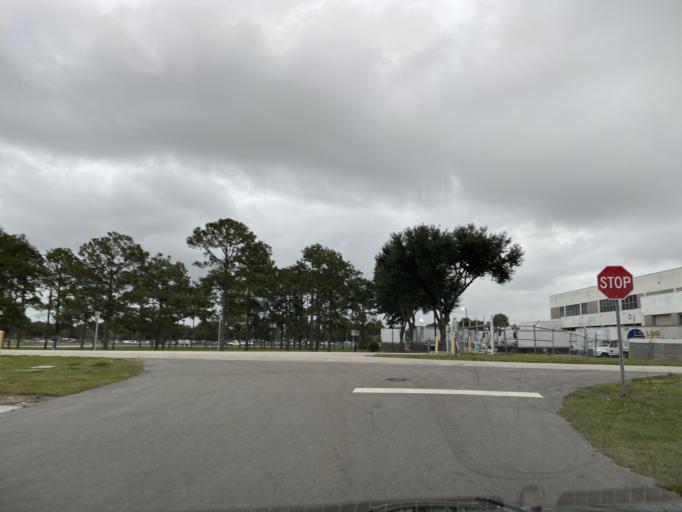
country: US
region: Florida
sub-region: Orange County
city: Belle Isle
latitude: 28.4427
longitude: -81.3173
